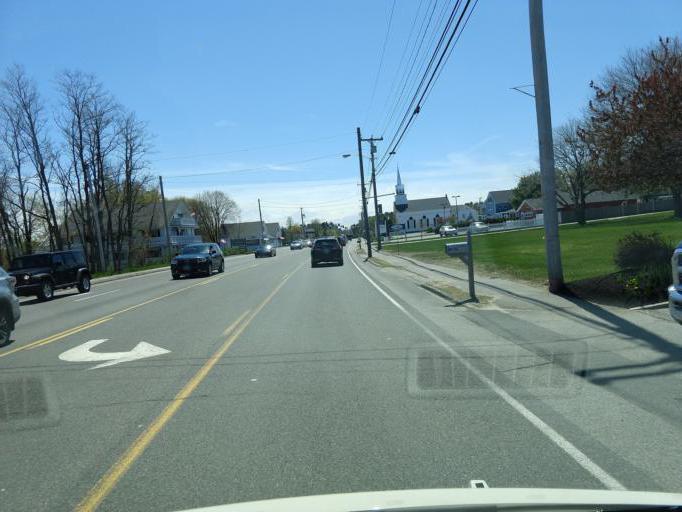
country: US
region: Maine
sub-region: York County
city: Wells Beach Station
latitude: 43.3031
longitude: -70.5855
